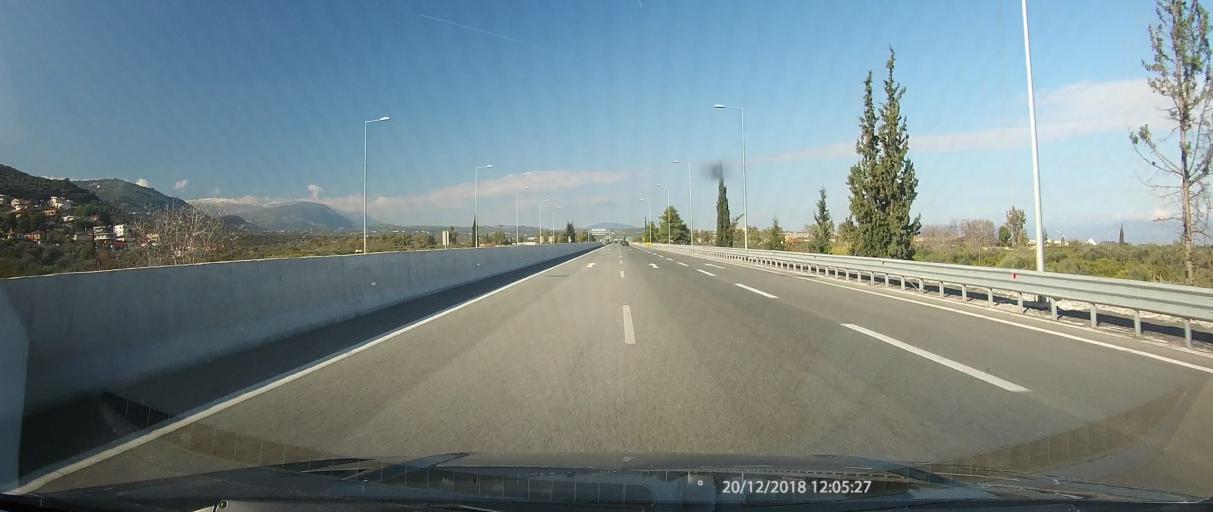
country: GR
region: West Greece
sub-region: Nomos Achaias
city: Temeni
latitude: 38.2231
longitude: 22.0994
